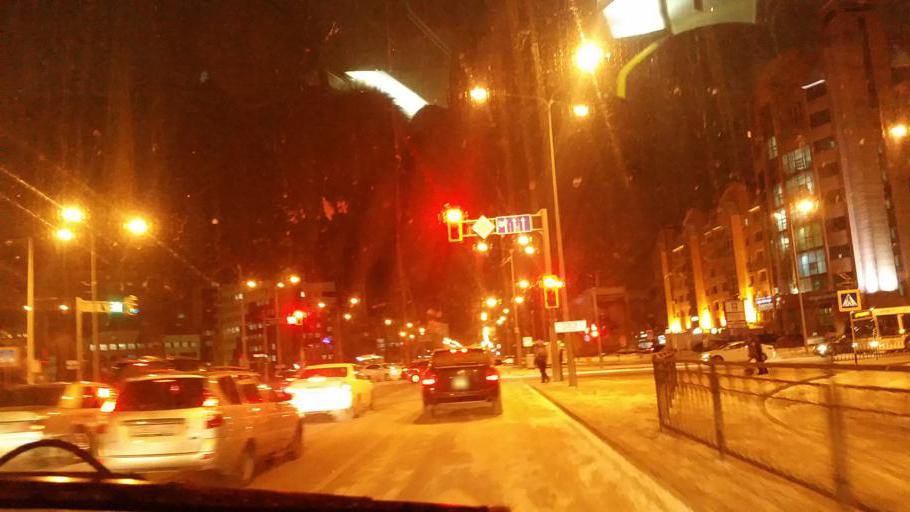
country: KZ
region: Astana Qalasy
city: Astana
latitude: 51.1538
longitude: 71.4662
